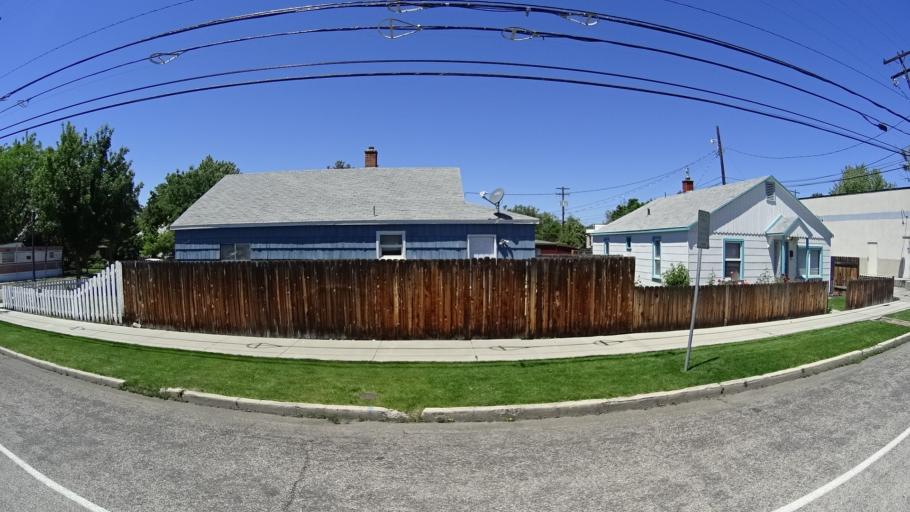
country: US
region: Idaho
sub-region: Ada County
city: Boise
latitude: 43.6133
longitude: -116.2110
